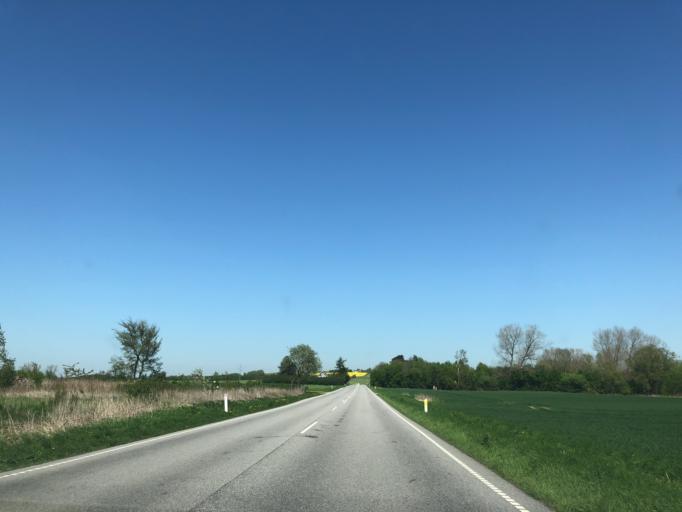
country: DK
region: Zealand
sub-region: Slagelse Kommune
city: Skaelskor
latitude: 55.3147
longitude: 11.2964
